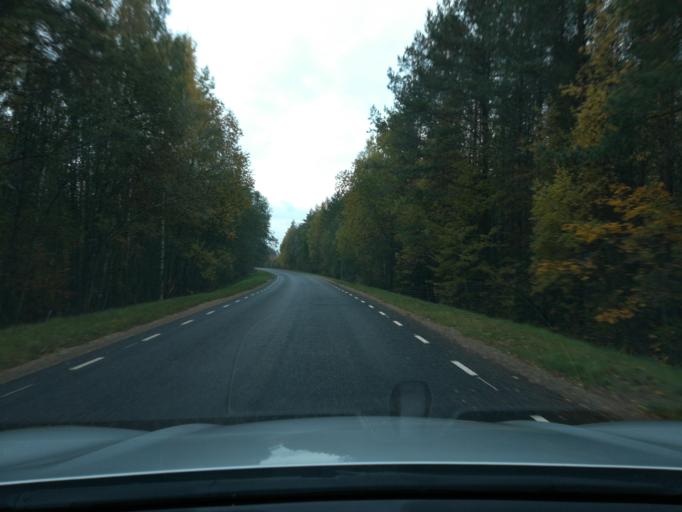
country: EE
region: Ida-Virumaa
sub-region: Johvi vald
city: Johvi
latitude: 59.0275
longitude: 27.3924
